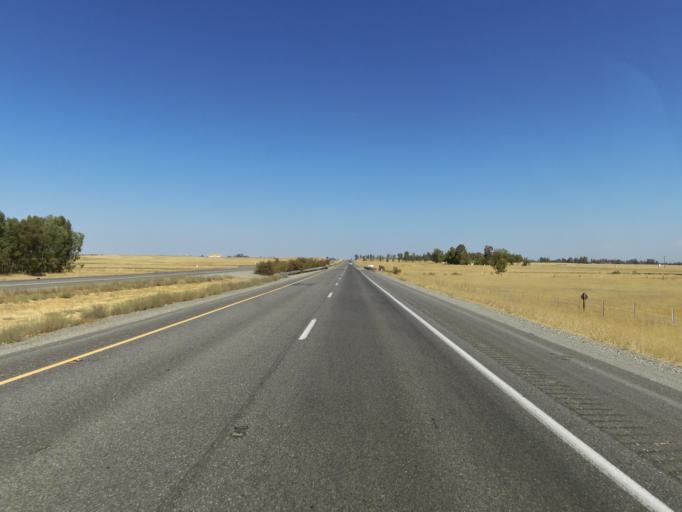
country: US
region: California
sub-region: Tehama County
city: Corning
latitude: 39.8548
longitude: -122.1999
